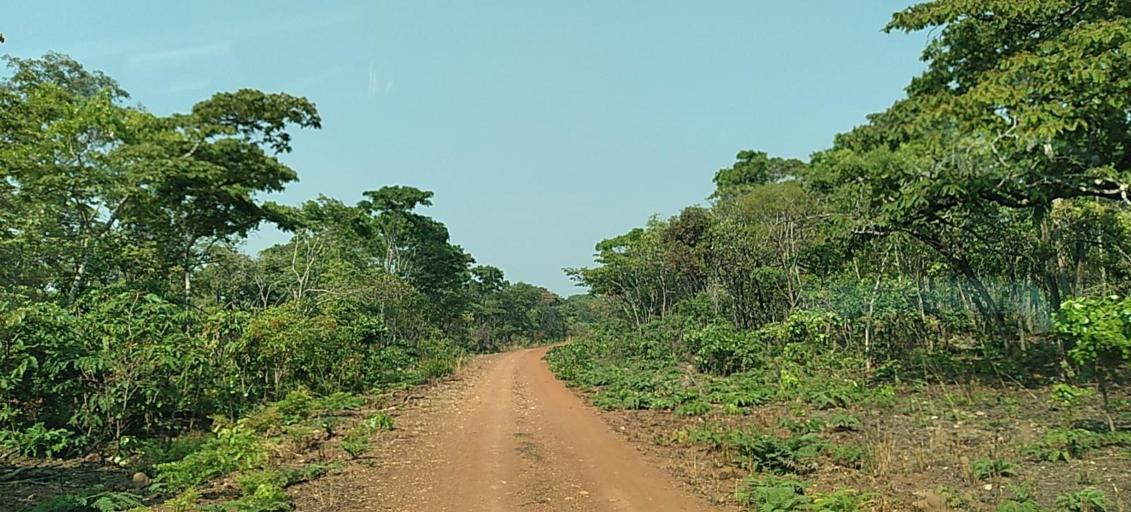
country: ZM
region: Copperbelt
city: Chingola
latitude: -12.8788
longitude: 27.4430
